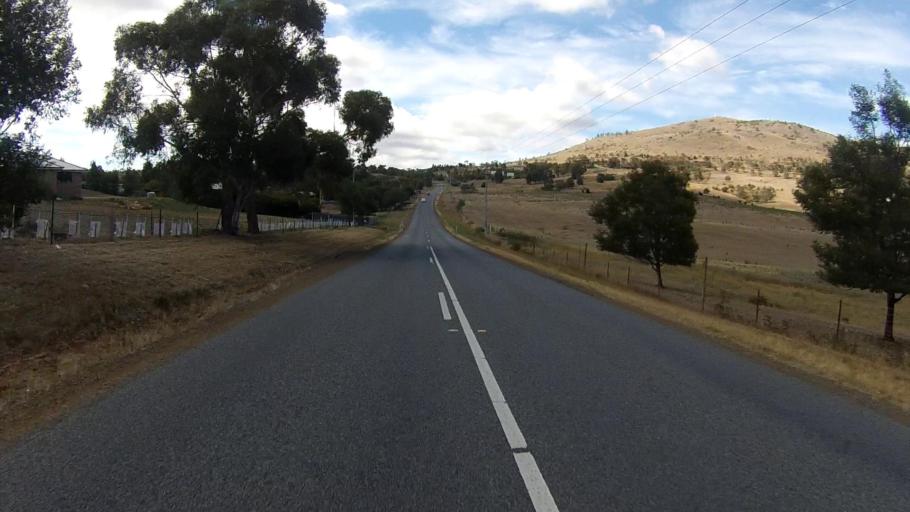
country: AU
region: Tasmania
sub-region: Glenorchy
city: Austins Ferry
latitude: -42.7222
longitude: 147.2811
